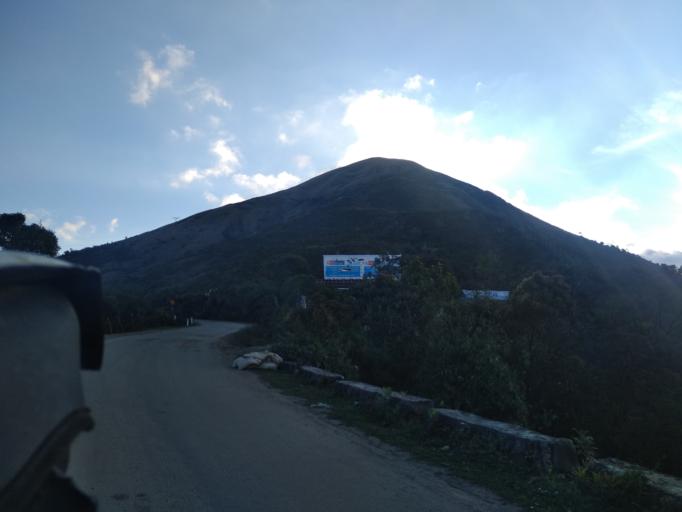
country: PE
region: Amazonas
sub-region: Provincia de Chachapoyas
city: Montevideo
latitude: -6.7142
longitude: -77.8721
